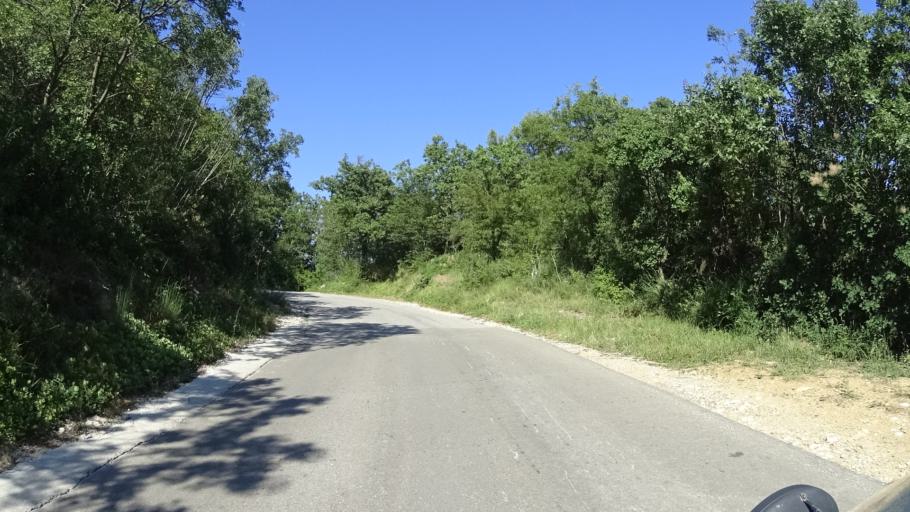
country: HR
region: Istarska
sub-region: Grad Labin
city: Labin
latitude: 45.0709
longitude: 14.1210
